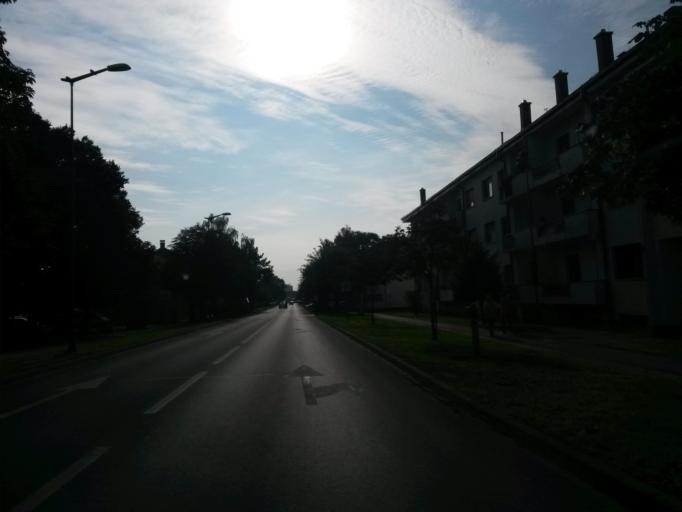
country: HR
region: Vukovarsko-Srijemska
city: Vukovar
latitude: 45.3567
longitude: 18.9936
